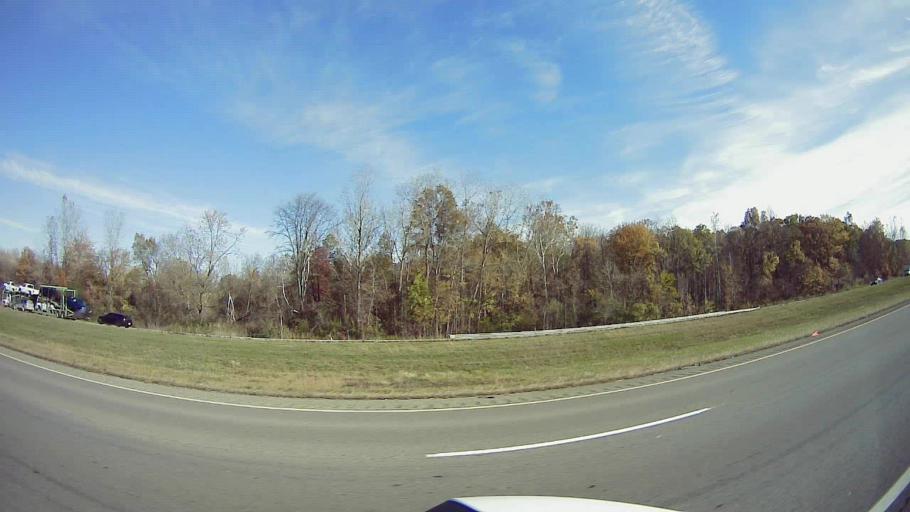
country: US
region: Michigan
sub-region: Wayne County
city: Romulus
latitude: 42.2315
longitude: -83.4334
